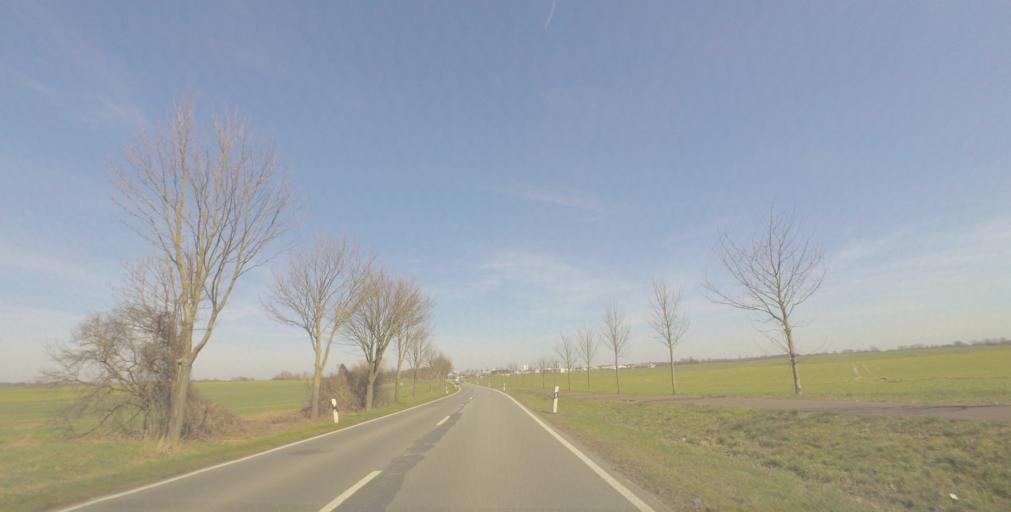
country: DE
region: Brandenburg
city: Neuruppin
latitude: 52.8719
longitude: 12.7835
